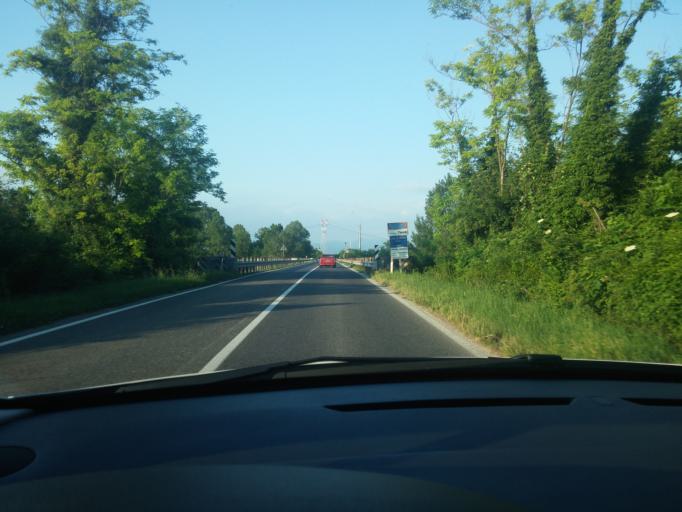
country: IT
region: Friuli Venezia Giulia
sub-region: Provincia di Udine
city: Ruda
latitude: 45.8504
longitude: 13.4184
